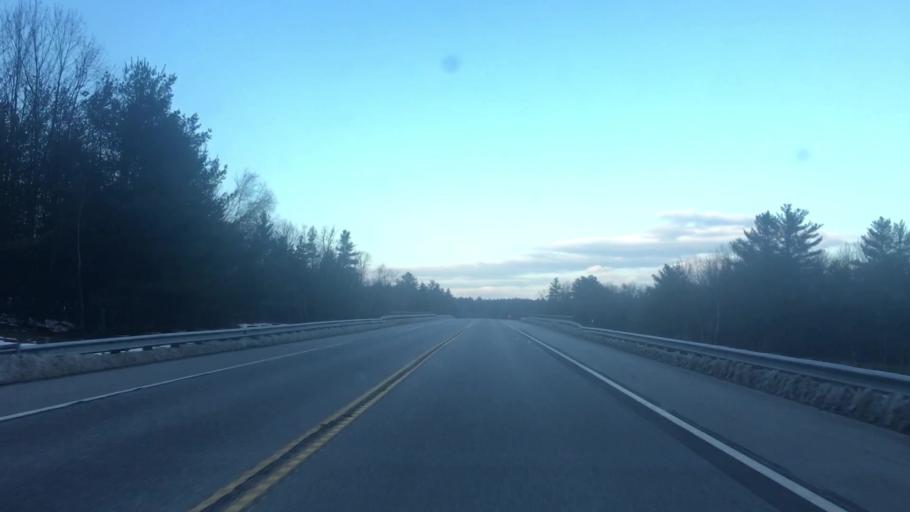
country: US
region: New Hampshire
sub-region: Hillsborough County
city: Hillsboro
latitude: 43.1352
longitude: -71.8814
